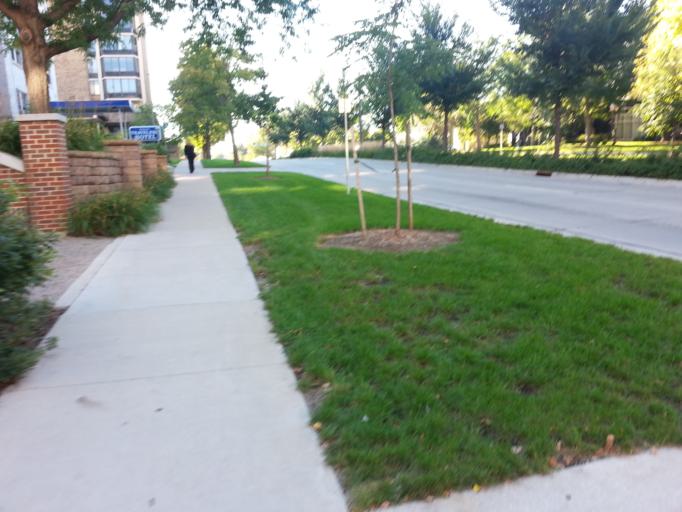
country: US
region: Minnesota
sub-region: Olmsted County
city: Rochester
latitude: 44.0216
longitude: -92.4690
